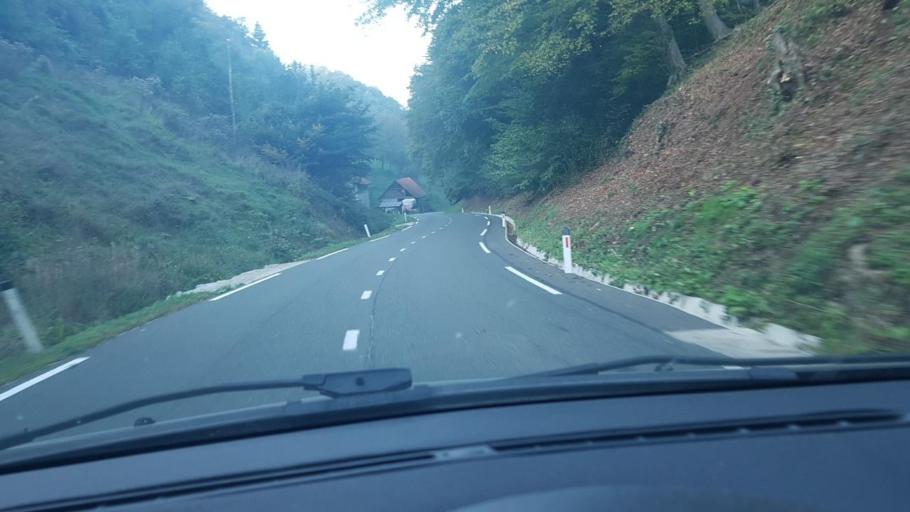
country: SI
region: Rogatec
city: Rogatec
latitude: 46.2702
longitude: 15.7123
